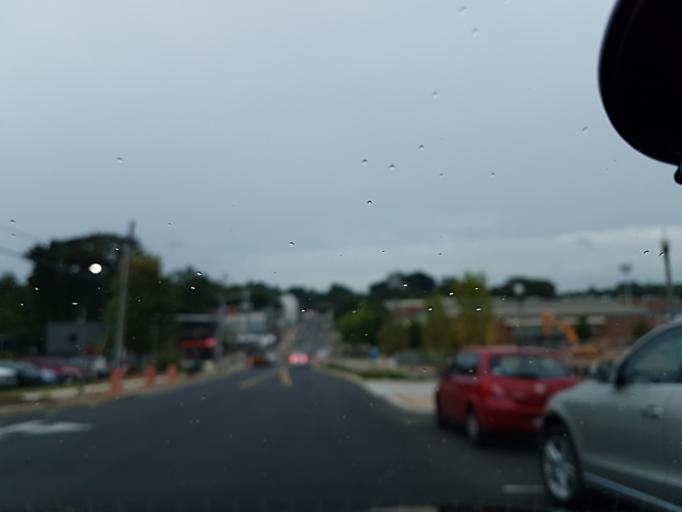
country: US
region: Georgia
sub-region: DeKalb County
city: Decatur
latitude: 33.7734
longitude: -84.2965
